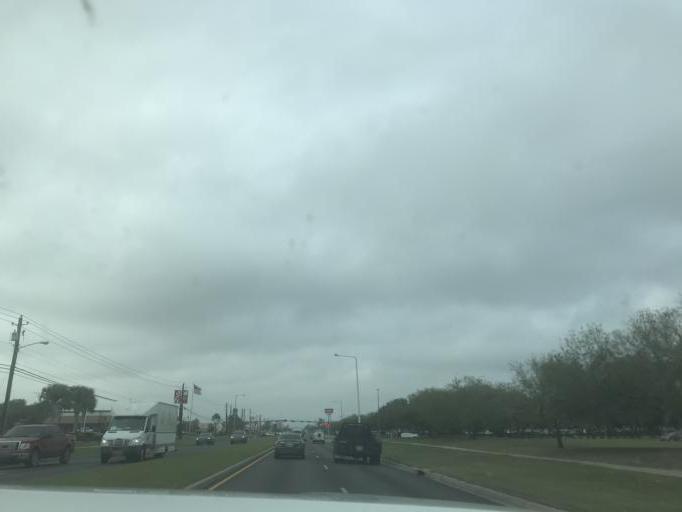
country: US
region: Texas
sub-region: Nueces County
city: Corpus Christi
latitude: 27.6821
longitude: -97.3769
